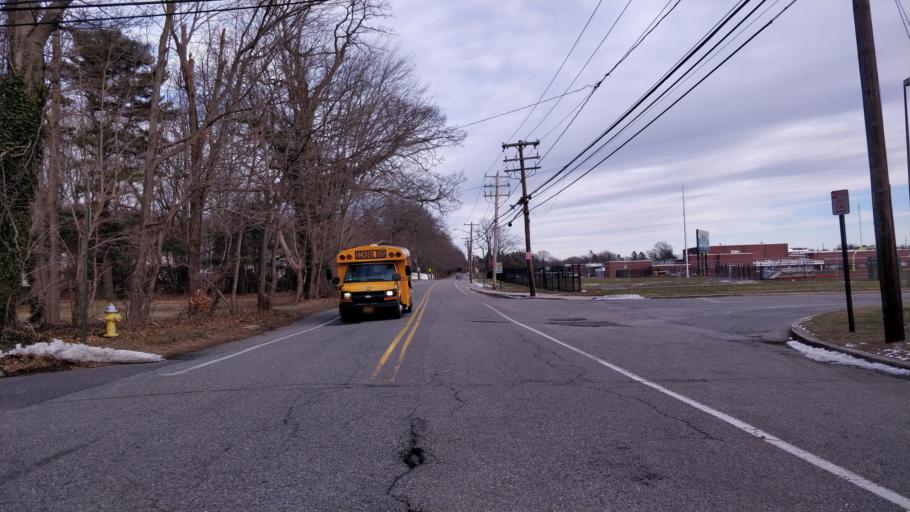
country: US
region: New York
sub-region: Suffolk County
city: Northport
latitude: 40.8800
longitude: -73.3457
